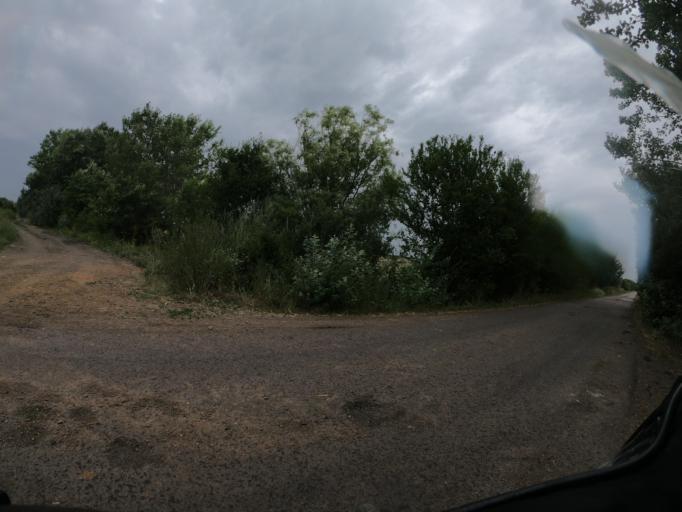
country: HU
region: Heves
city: Poroszlo
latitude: 47.6753
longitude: 20.5678
